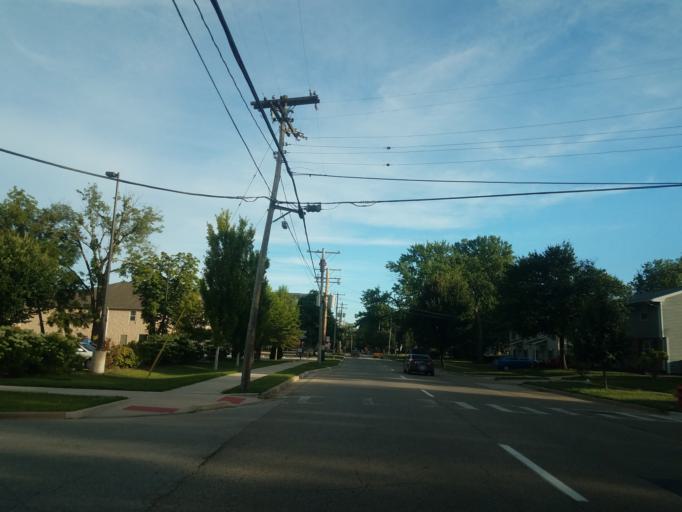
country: US
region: Illinois
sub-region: McLean County
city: Normal
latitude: 40.5057
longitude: -88.9965
